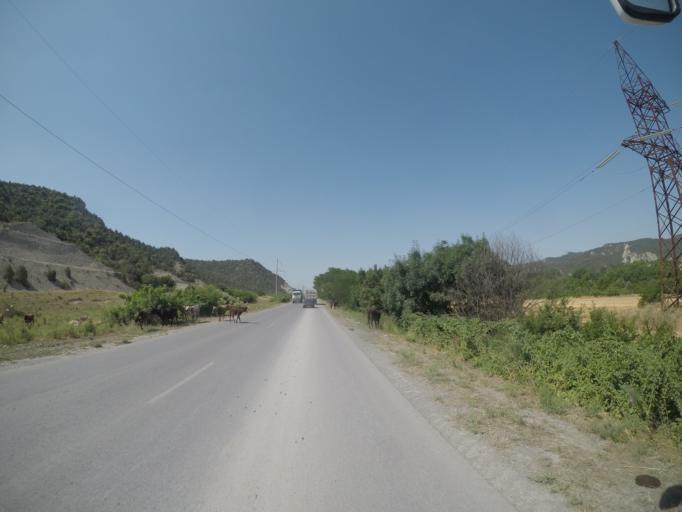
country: AZ
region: Agdas
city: Agdas
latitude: 40.7381
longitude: 47.5796
